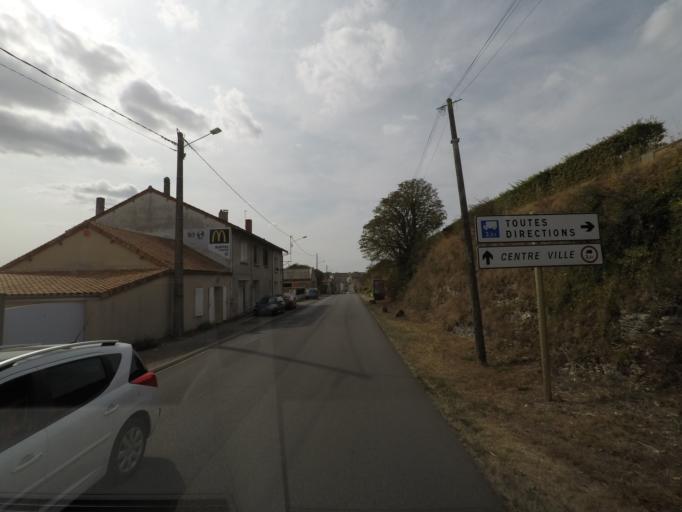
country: FR
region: Poitou-Charentes
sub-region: Departement de la Charente
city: Ruffec
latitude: 46.0275
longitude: 0.2087
